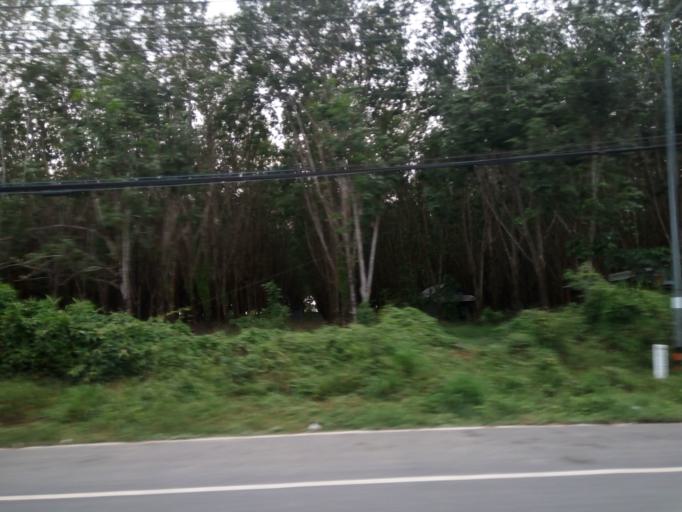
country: TH
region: Phuket
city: Mueang Phuket
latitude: 7.8476
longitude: 98.3822
